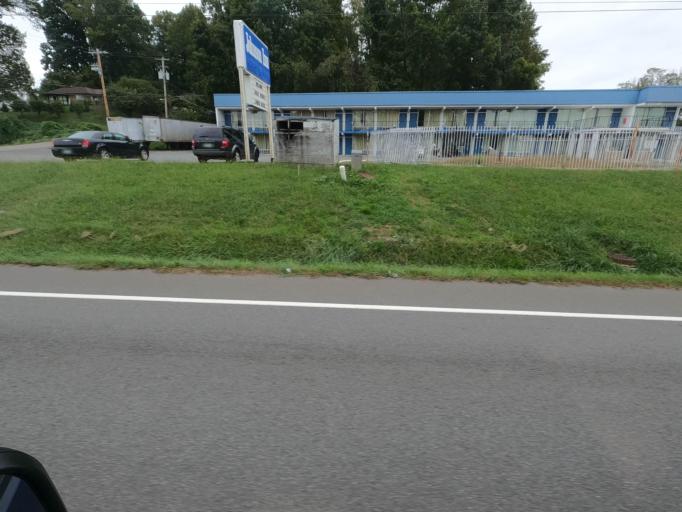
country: US
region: Tennessee
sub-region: Washington County
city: Midway
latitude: 36.3096
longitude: -82.3964
